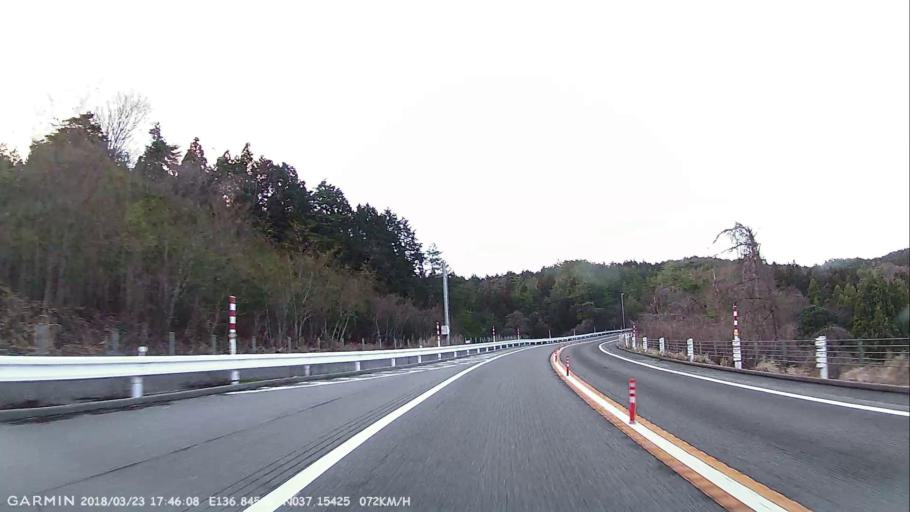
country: JP
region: Ishikawa
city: Nanao
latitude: 37.1545
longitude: 136.8456
